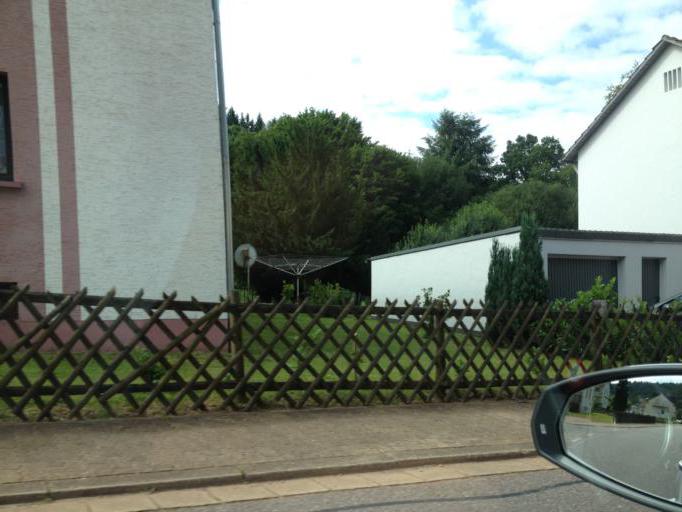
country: DE
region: Saarland
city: Mettlach
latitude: 49.4935
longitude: 6.6128
